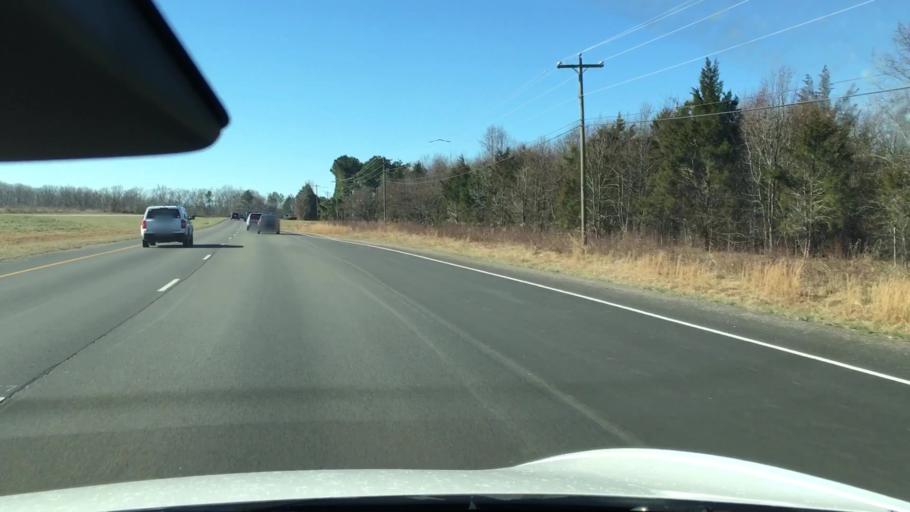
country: US
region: Virginia
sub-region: Chesterfield County
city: Woodlake
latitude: 37.5111
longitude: -77.7013
